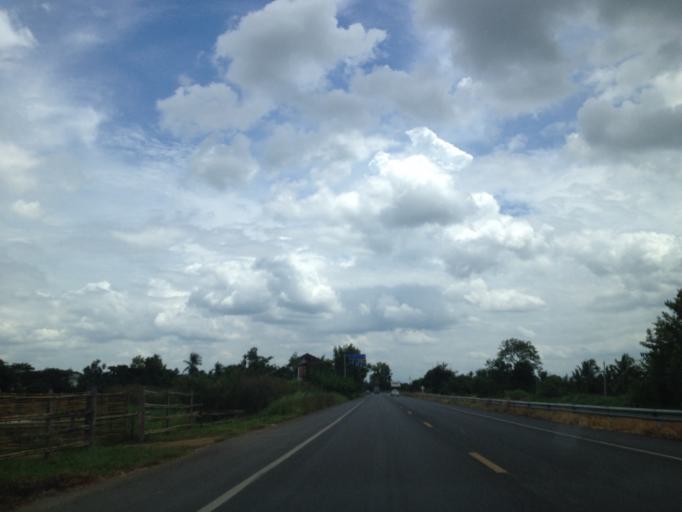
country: TH
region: Chiang Mai
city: San Pa Tong
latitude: 18.6343
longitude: 98.8599
